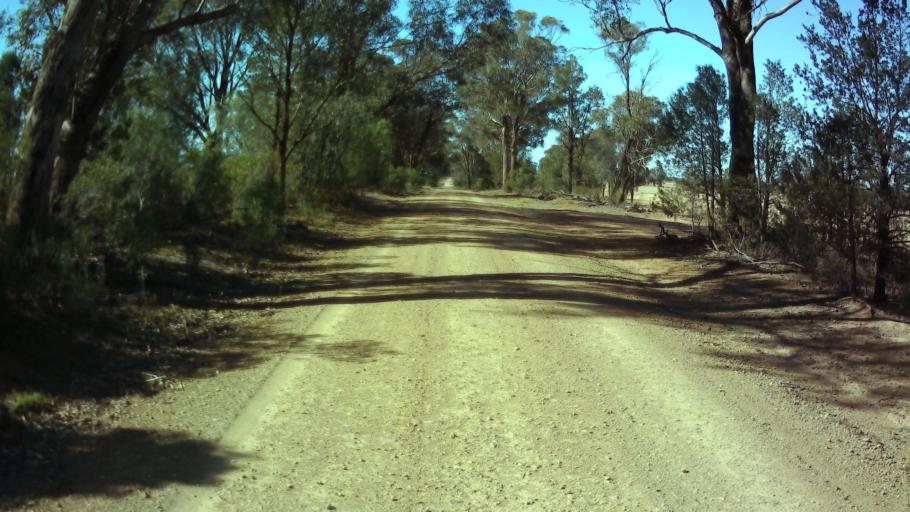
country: AU
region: New South Wales
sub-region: Weddin
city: Grenfell
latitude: -33.9129
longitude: 147.8763
